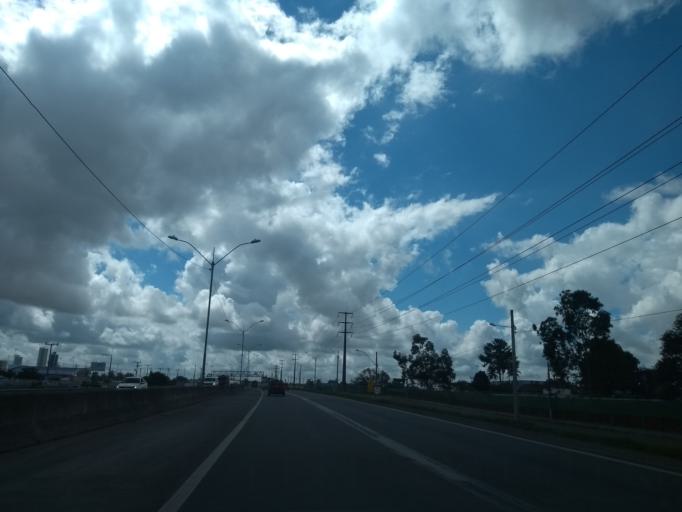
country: BR
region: Bahia
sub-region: Feira De Santana
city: Feira de Santana
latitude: -12.2768
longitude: -38.9391
